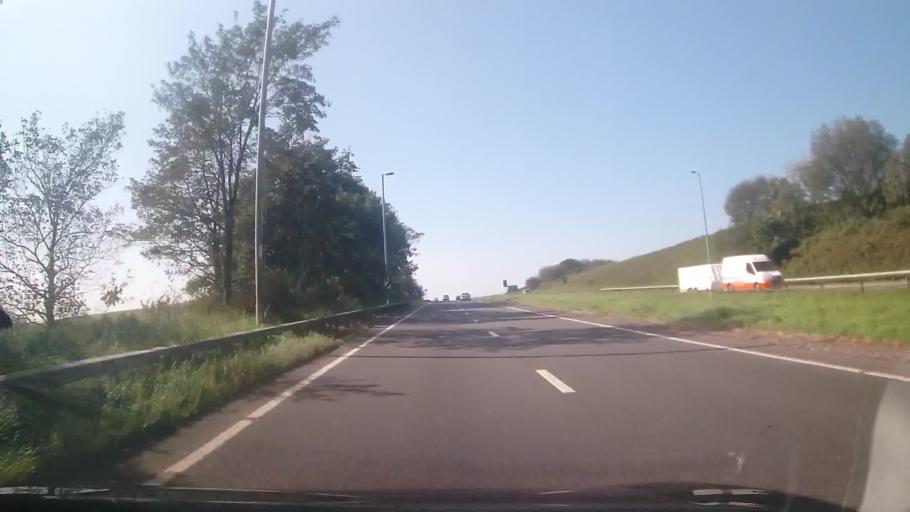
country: GB
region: Wales
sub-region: Carmarthenshire
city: Llangynog
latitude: 51.8298
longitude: -4.4417
